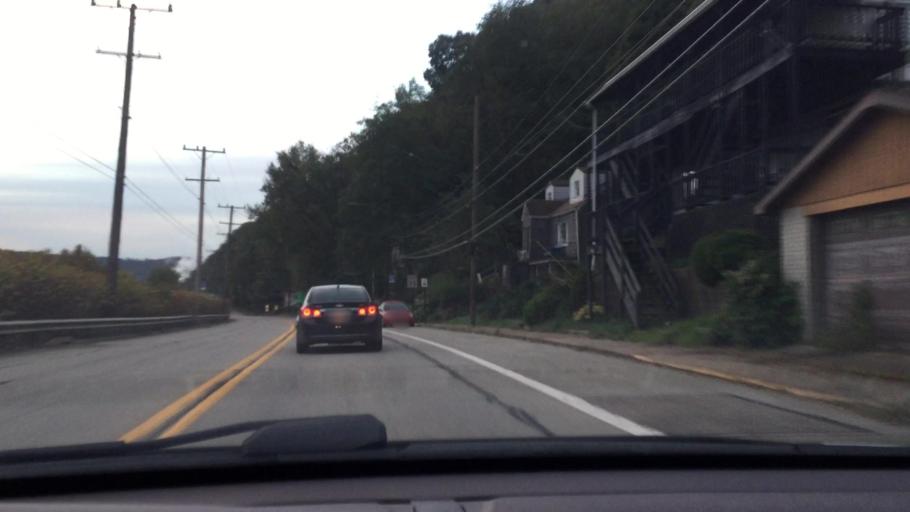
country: US
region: Pennsylvania
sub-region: Westmoreland County
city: New Kensington
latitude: 40.5684
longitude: -79.7764
